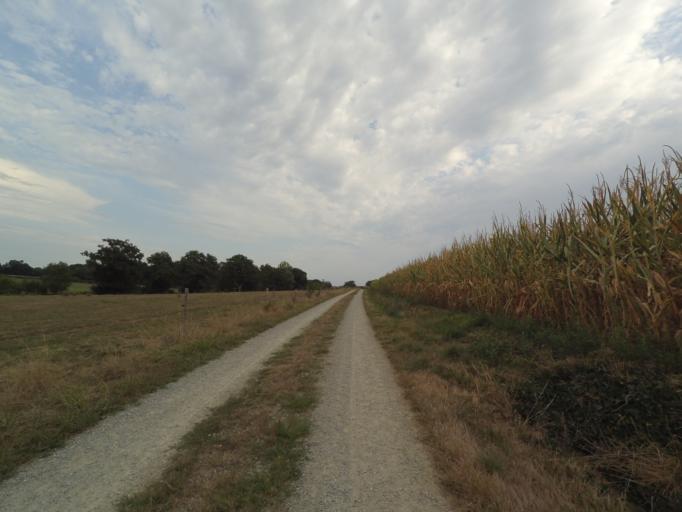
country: FR
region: Pays de la Loire
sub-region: Departement de la Vendee
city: Bouffere
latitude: 46.9848
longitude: -1.3701
